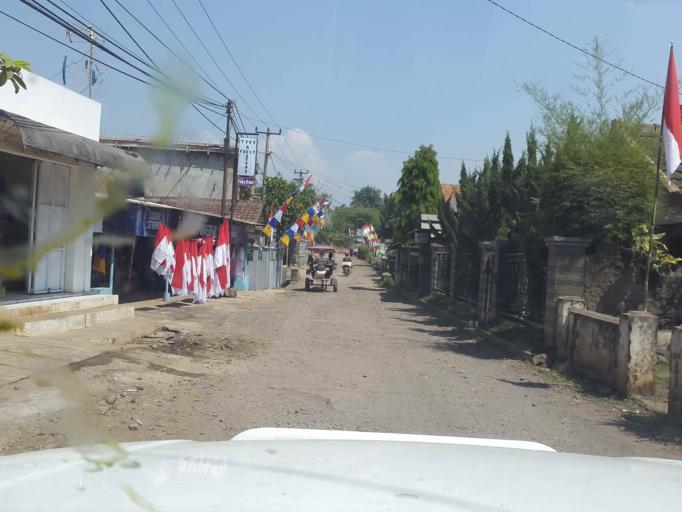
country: ID
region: West Java
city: Ciranjang-hilir
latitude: -6.8609
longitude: 107.2411
